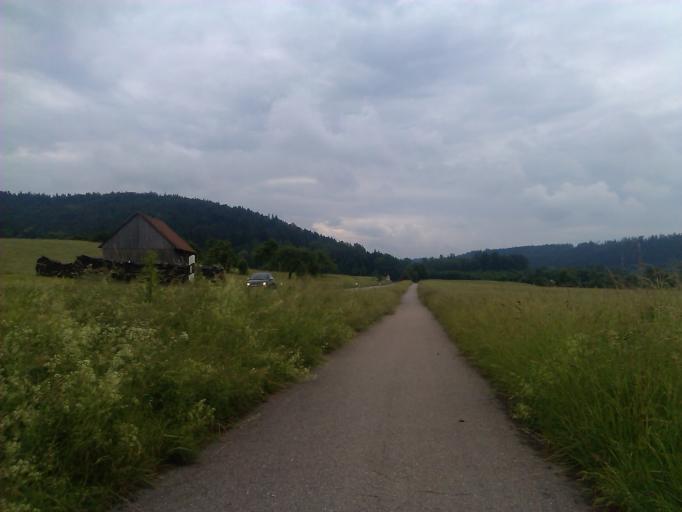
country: DE
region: Baden-Wuerttemberg
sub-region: Regierungsbezirk Stuttgart
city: Oberrot
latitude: 49.0002
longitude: 9.6843
